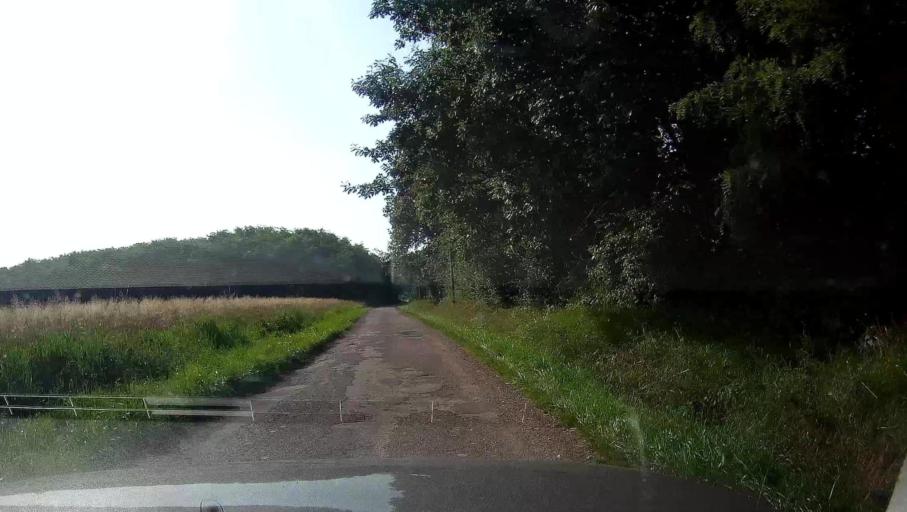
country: FR
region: Bourgogne
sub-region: Departement de Saone-et-Loire
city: Saint-Leger-sur-Dheune
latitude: 46.8753
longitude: 4.6306
